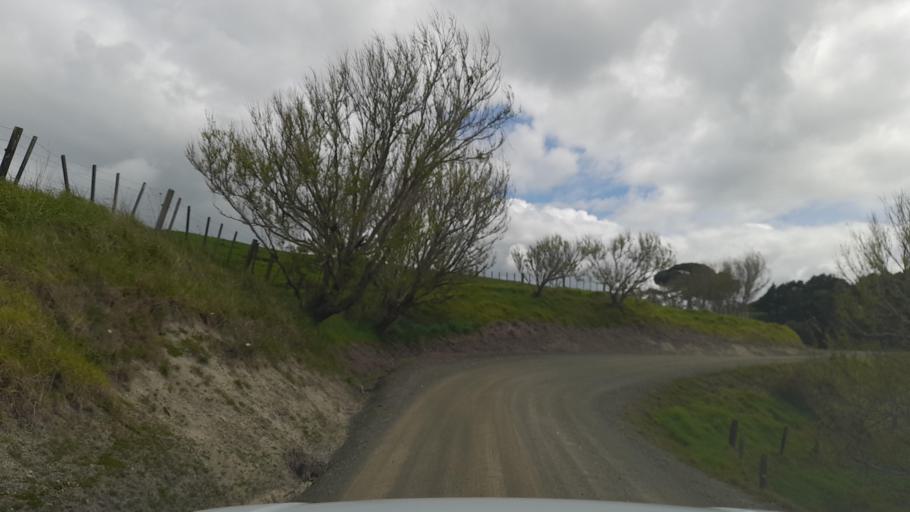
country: NZ
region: Auckland
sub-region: Auckland
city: Wellsford
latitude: -36.2180
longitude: 174.3212
